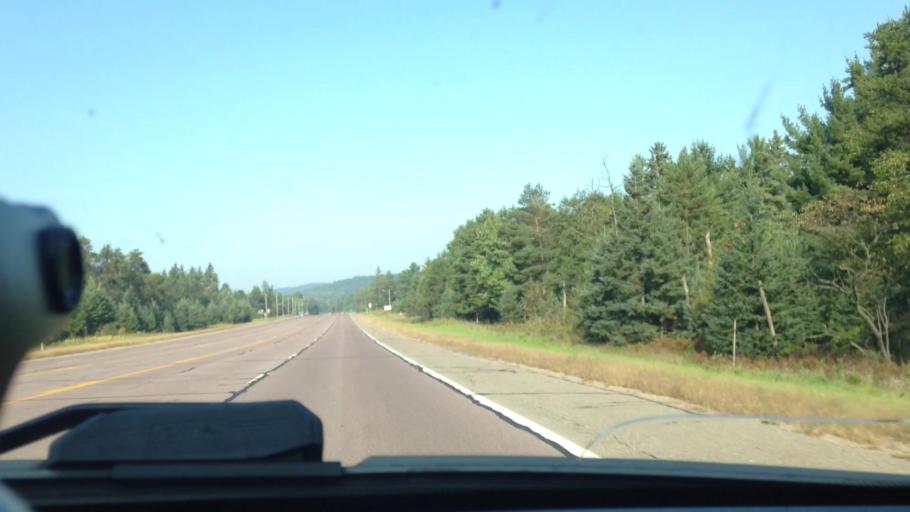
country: US
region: Michigan
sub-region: Dickinson County
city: Quinnesec
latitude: 45.8013
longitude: -87.9546
